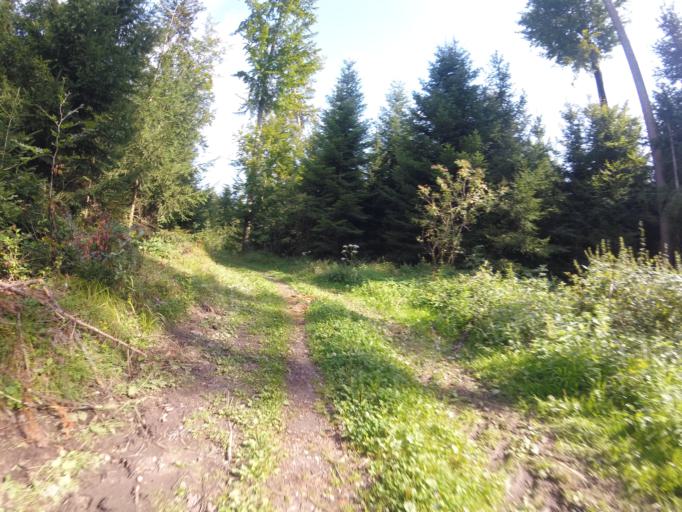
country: DE
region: Baden-Wuerttemberg
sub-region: Regierungsbezirk Stuttgart
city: Sulzbach an der Murr
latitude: 48.9706
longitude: 9.5177
